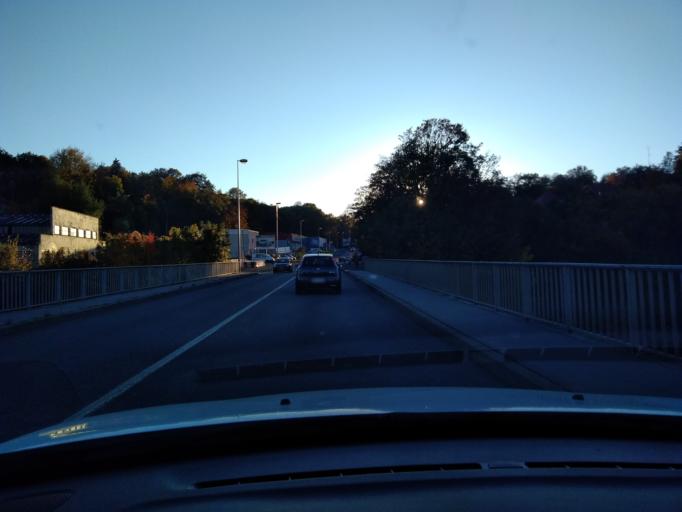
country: FR
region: Lorraine
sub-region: Departement de la Moselle
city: Sarreguemines
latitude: 49.1027
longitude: 7.0720
